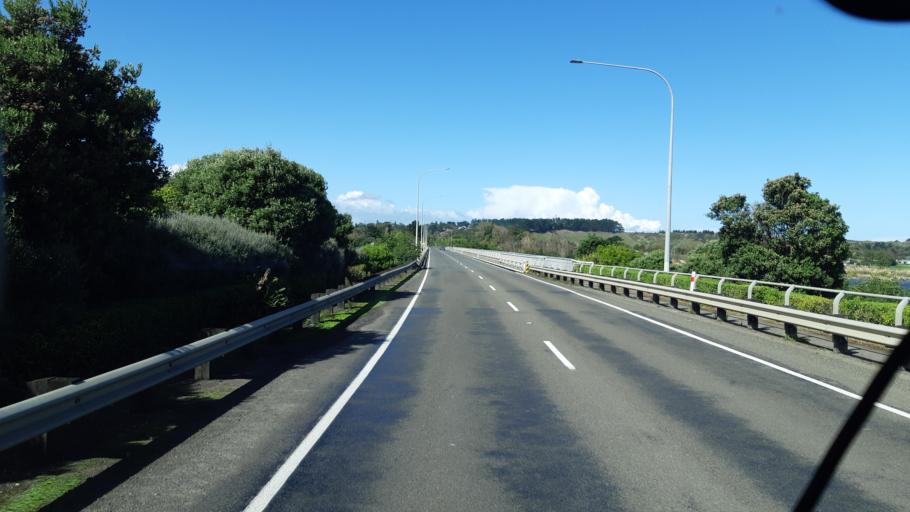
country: NZ
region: Manawatu-Wanganui
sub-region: Wanganui District
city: Wanganui
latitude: -39.9438
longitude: 175.0446
